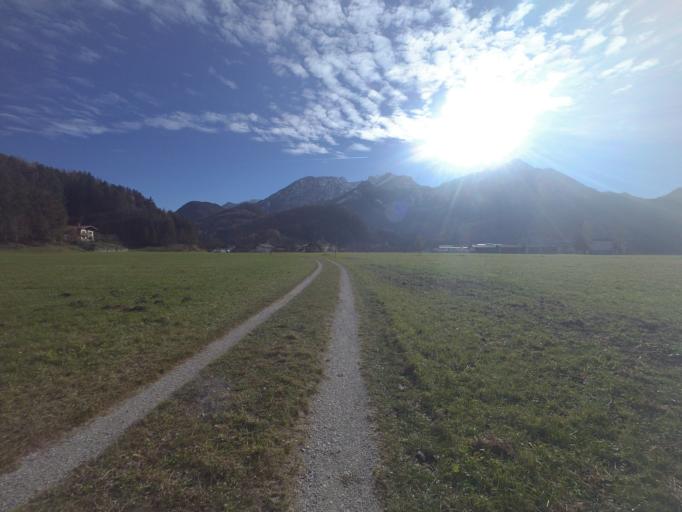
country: AT
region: Salzburg
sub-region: Politischer Bezirk Hallein
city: Golling an der Salzach
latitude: 47.5938
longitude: 13.1804
